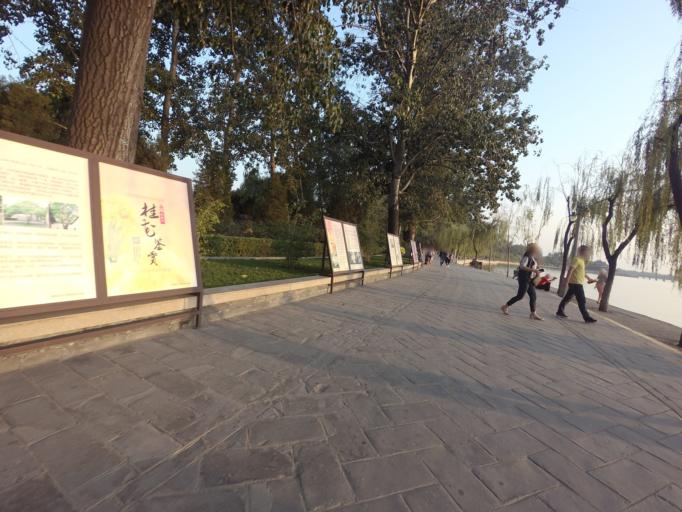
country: CN
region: Beijing
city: Haidian
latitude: 39.9936
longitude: 116.2743
